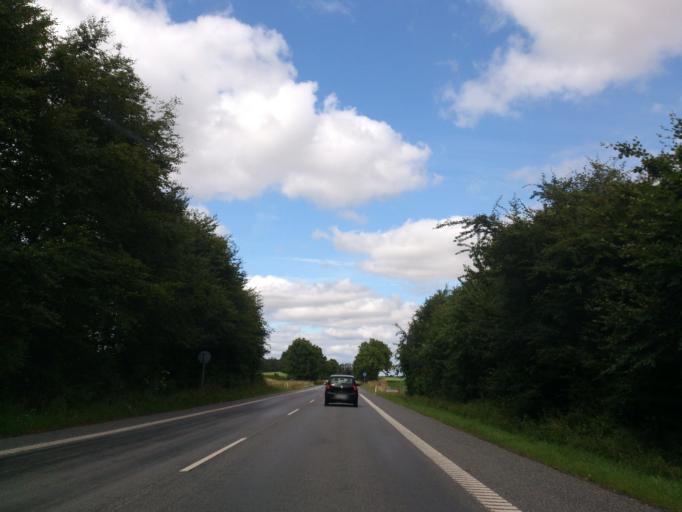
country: DK
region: South Denmark
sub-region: Aabenraa Kommune
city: Krusa
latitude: 54.9023
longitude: 9.4356
